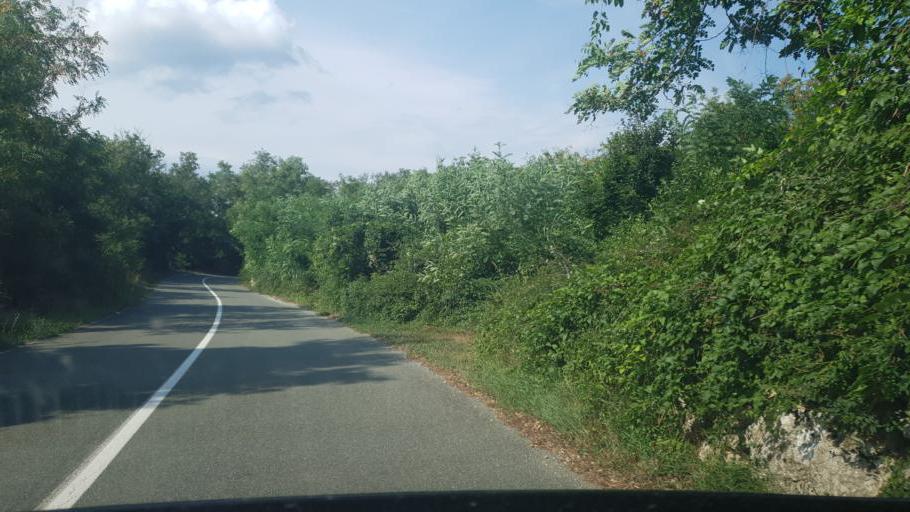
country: HR
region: Primorsko-Goranska
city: Punat
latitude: 45.1008
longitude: 14.6419
